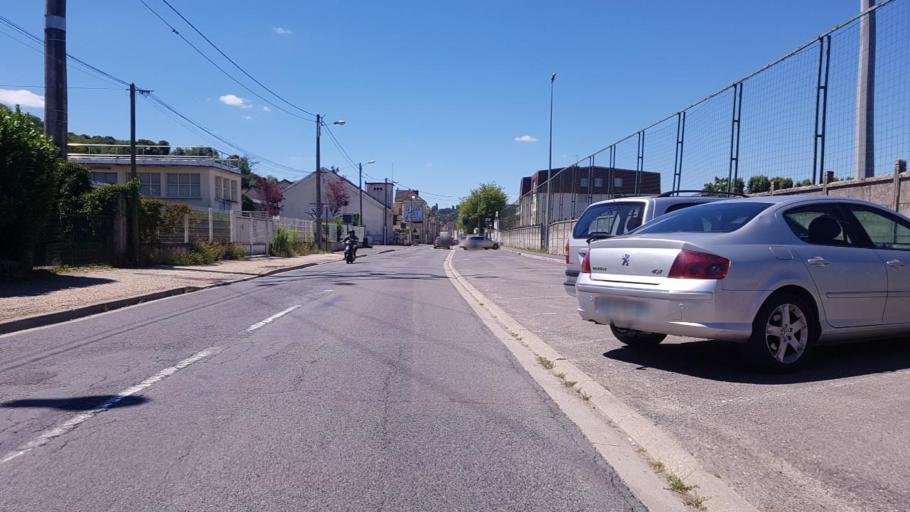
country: FR
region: Ile-de-France
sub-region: Departement de Seine-et-Marne
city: La Ferte-sous-Jouarre
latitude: 48.9515
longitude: 3.1376
